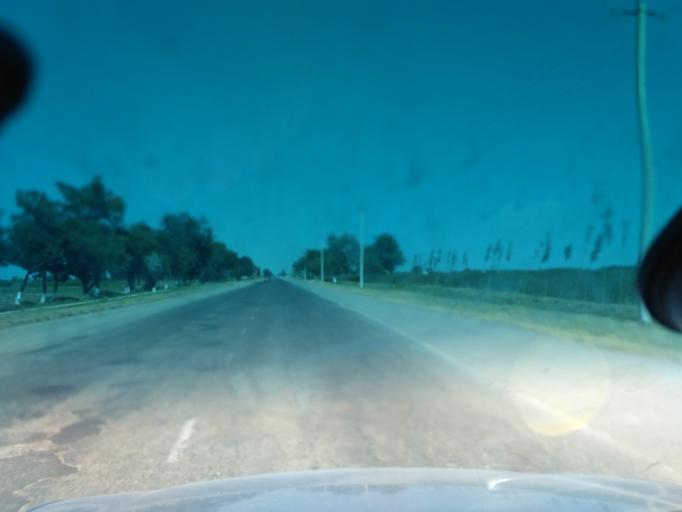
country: UZ
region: Sirdaryo
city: Guliston
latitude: 40.4962
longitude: 68.9321
